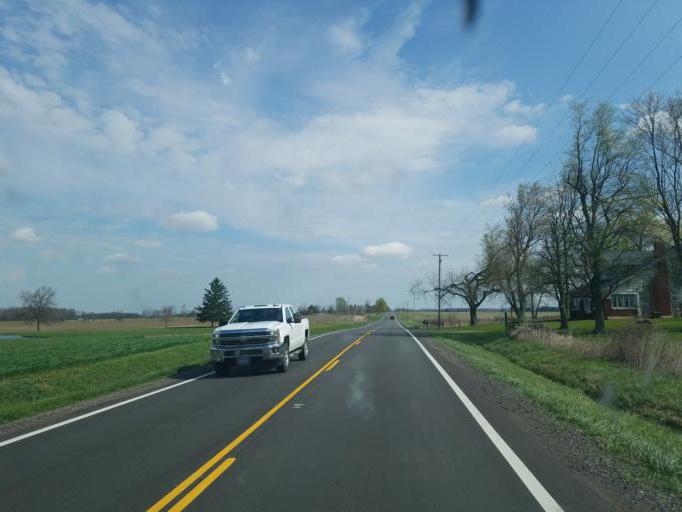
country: US
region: Ohio
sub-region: Marion County
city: Marion
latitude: 40.6577
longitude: -83.0176
